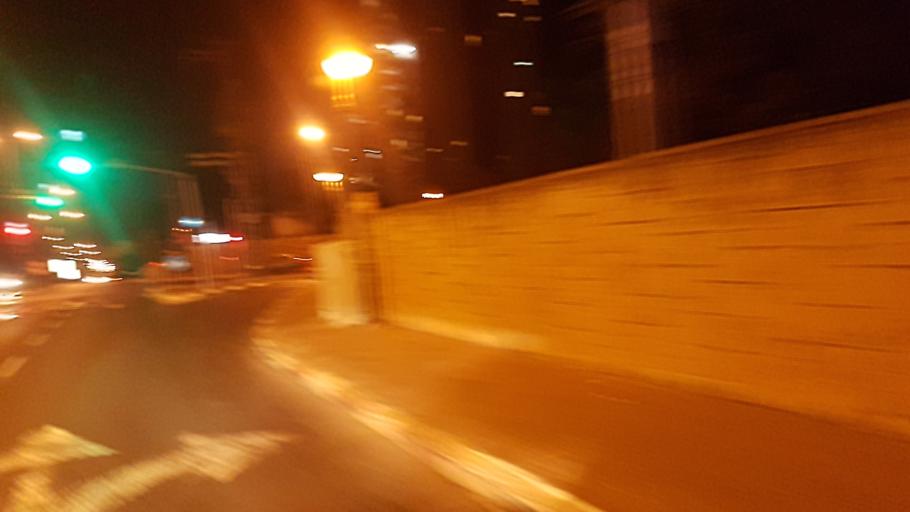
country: IL
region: Central District
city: Hod HaSharon
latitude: 32.1634
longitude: 34.8940
